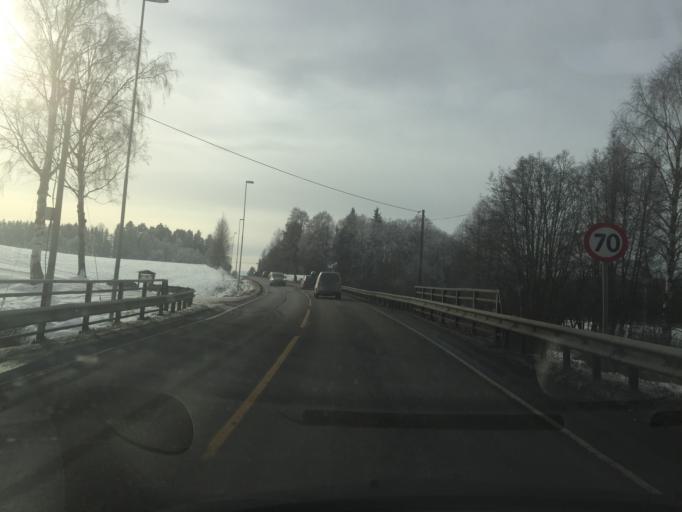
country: NO
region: Hedmark
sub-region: Loten
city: Loten
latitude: 60.8134
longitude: 11.3083
